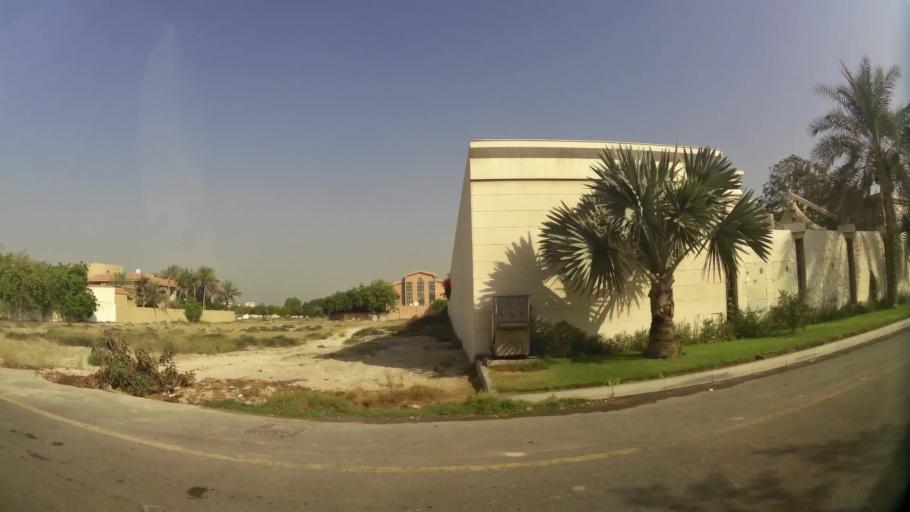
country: AE
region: Ash Shariqah
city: Sharjah
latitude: 25.3100
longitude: 55.3447
